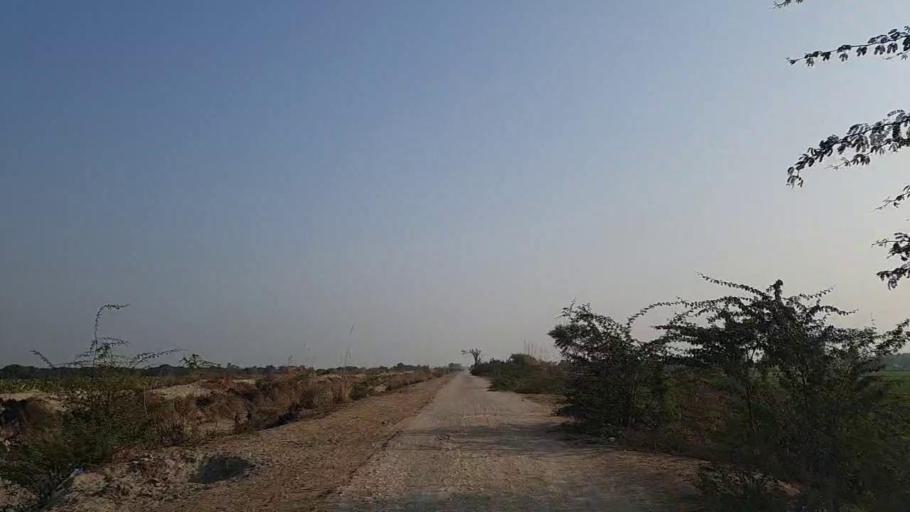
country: PK
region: Sindh
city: Jam Sahib
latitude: 26.2353
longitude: 68.5927
